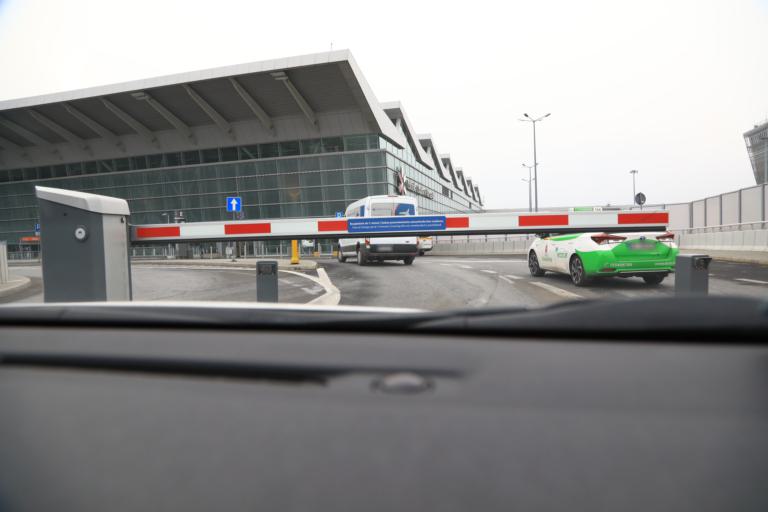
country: PL
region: Masovian Voivodeship
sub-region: Warszawa
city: Wlochy
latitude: 52.1733
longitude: 20.9724
